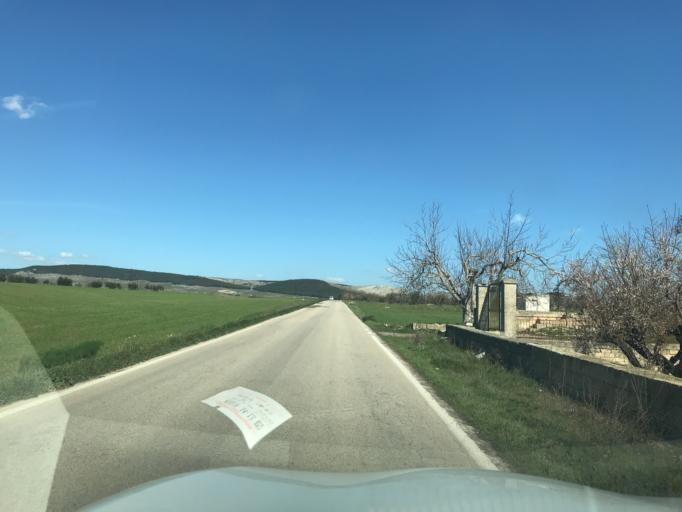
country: IT
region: Apulia
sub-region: Provincia di Bari
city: Gravina in Puglia
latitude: 40.8504
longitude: 16.4289
